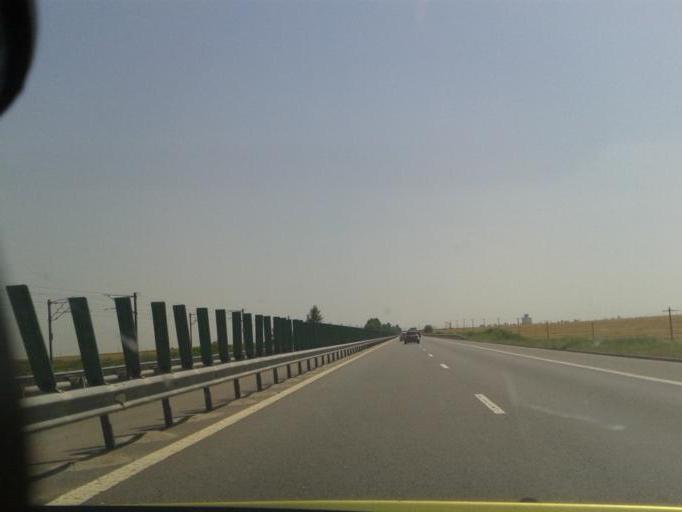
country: RO
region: Calarasi
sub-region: Comuna Sarulesti
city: Sarulesti-Gara
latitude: 44.4485
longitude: 26.6030
